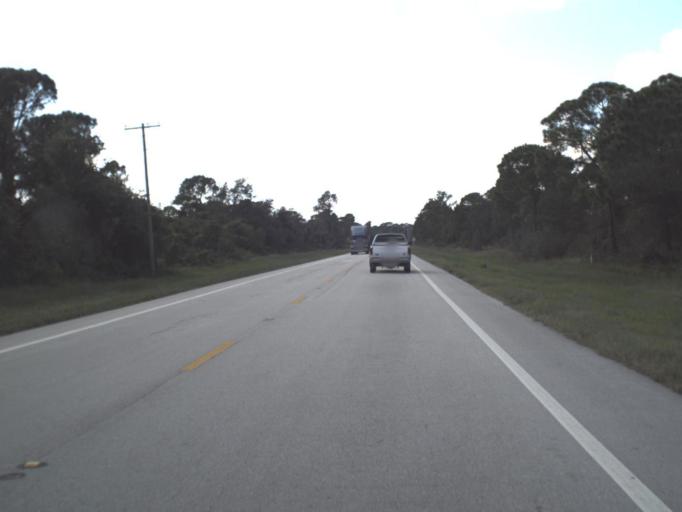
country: US
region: Florida
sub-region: Highlands County
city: Sebring
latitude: 27.4191
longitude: -81.4400
